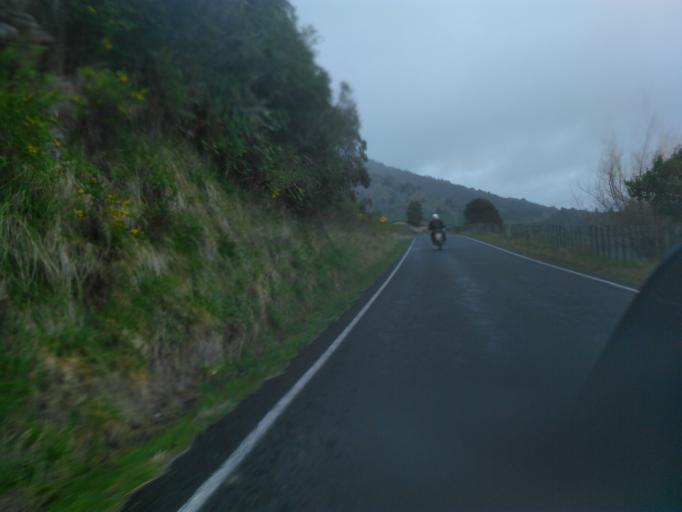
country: NZ
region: Gisborne
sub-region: Gisborne District
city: Gisborne
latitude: -38.6681
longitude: 177.7149
